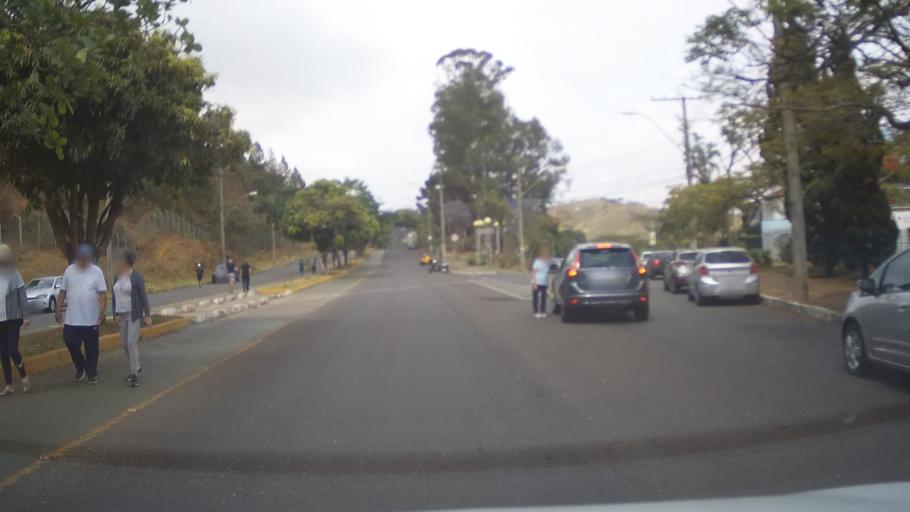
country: BR
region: Minas Gerais
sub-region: Belo Horizonte
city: Belo Horizonte
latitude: -19.9562
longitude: -43.9092
